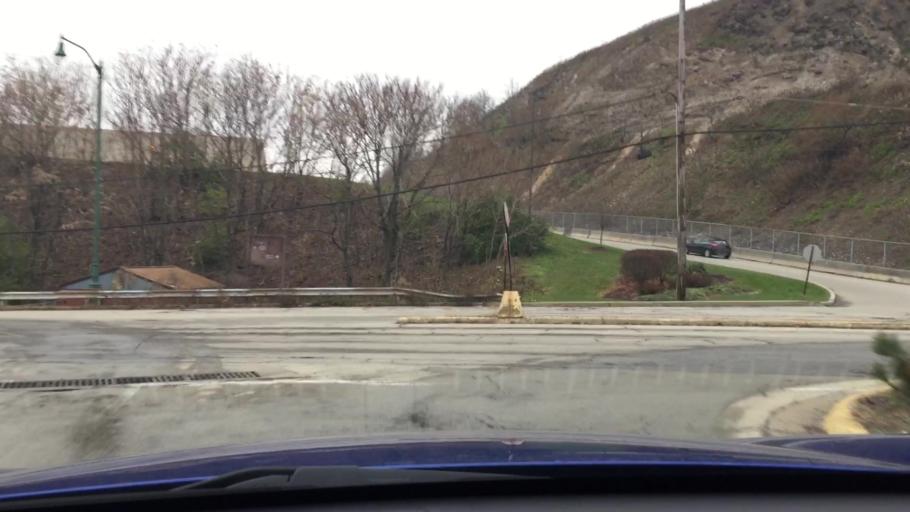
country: US
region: Pennsylvania
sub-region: Allegheny County
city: Pleasant Hills
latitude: 40.3385
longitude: -79.9479
